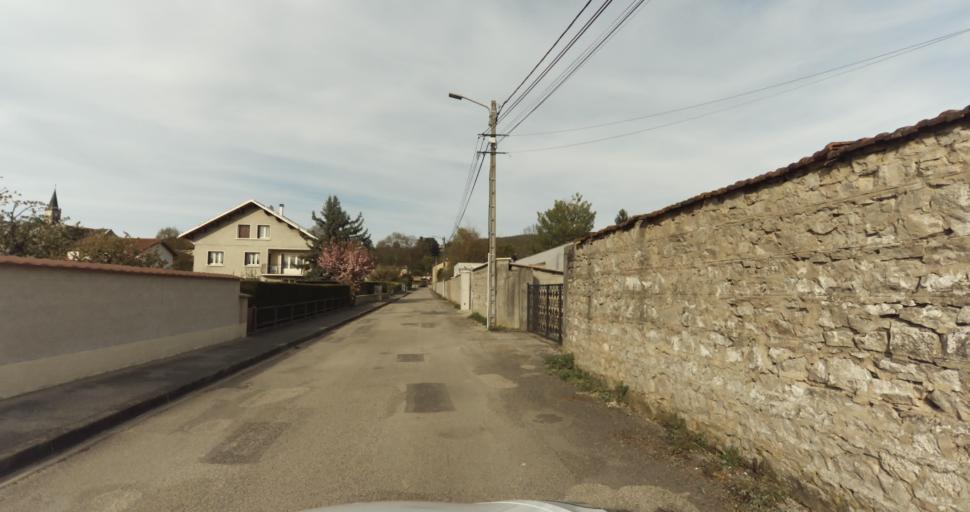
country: FR
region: Rhone-Alpes
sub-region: Departement de l'Ain
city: Amberieu-en-Bugey
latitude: 45.9542
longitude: 5.3580
